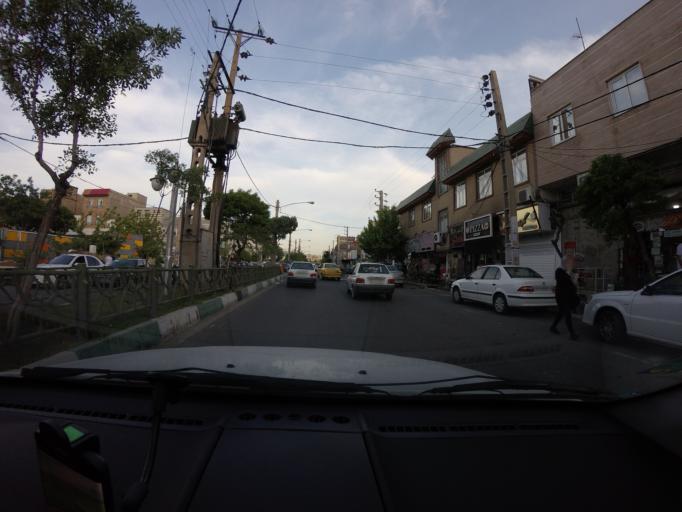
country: IR
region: Tehran
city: Eslamshahr
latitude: 35.5276
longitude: 51.2269
